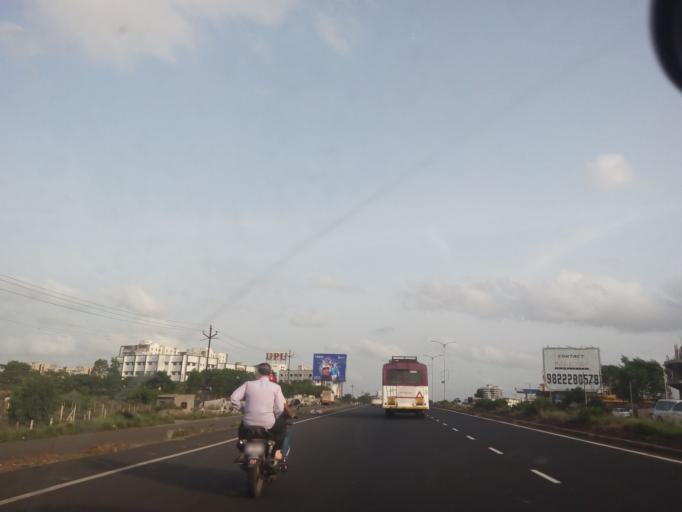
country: IN
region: Maharashtra
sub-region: Pune Division
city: Pimpri
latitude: 18.6179
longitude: 73.7475
